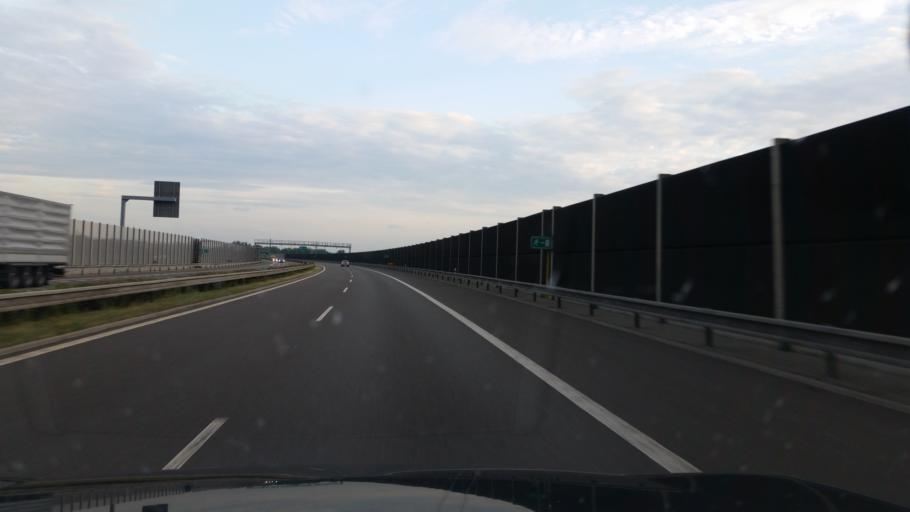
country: PL
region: Silesian Voivodeship
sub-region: Powiat raciborski
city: Chalupki
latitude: 49.8984
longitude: 18.3037
